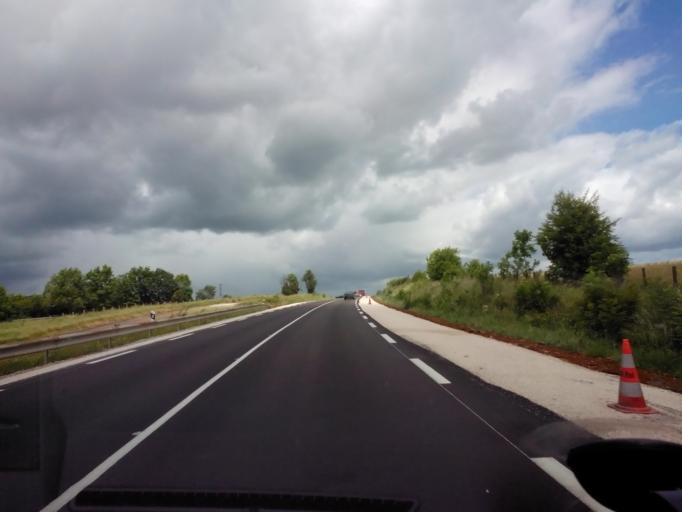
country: FR
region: Champagne-Ardenne
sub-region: Departement de la Haute-Marne
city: Rolampont
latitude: 47.9279
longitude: 5.2899
